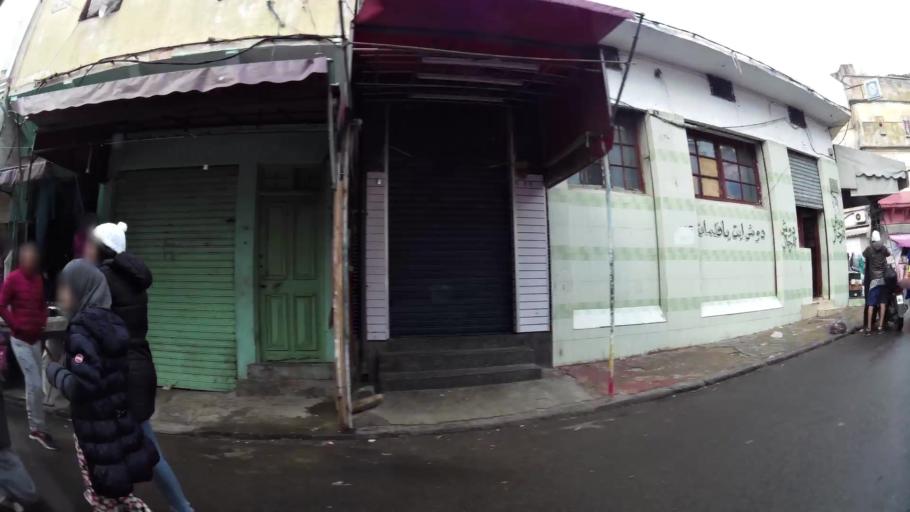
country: MA
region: Grand Casablanca
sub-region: Casablanca
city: Casablanca
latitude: 33.5726
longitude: -7.6030
